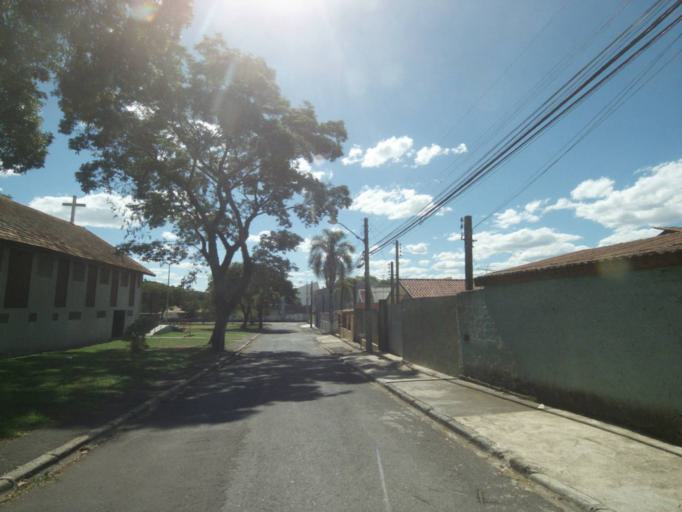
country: BR
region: Parana
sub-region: Curitiba
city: Curitiba
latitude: -25.5053
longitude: -49.3227
